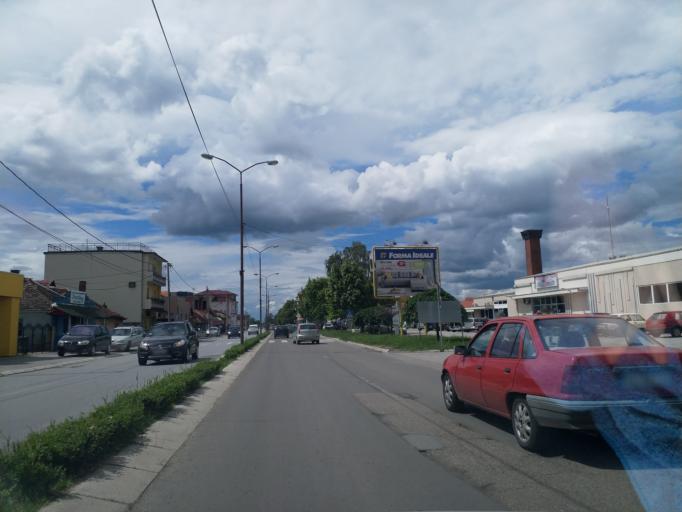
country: RS
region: Central Serbia
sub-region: Pomoravski Okrug
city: Paracin
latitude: 43.8660
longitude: 21.4071
